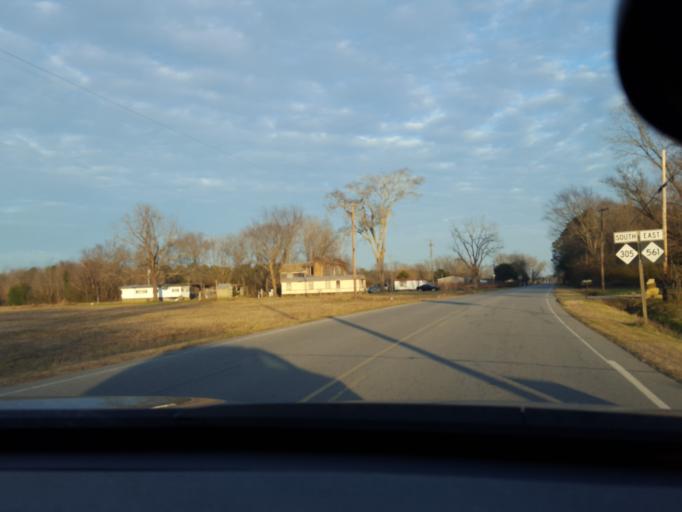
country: US
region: North Carolina
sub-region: Hertford County
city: Murfreesboro
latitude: 36.2707
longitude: -77.2344
